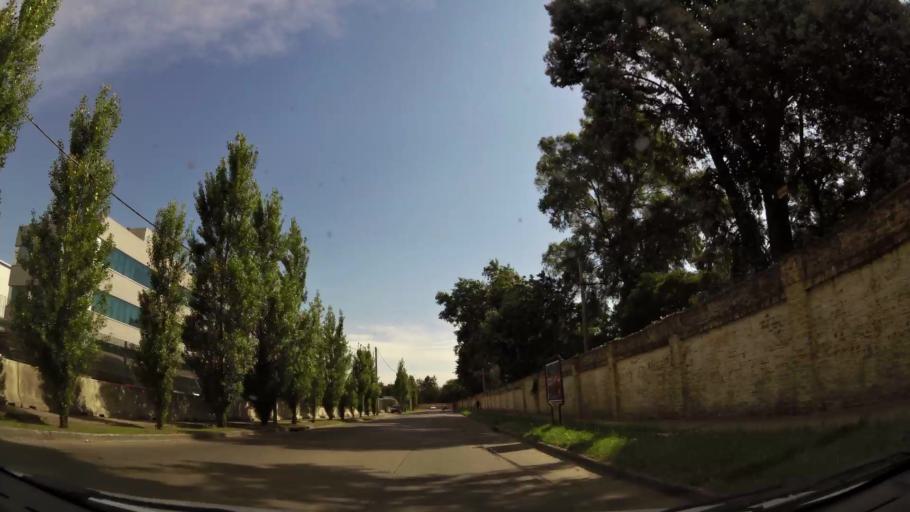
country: AR
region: Buenos Aires
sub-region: Partido de Merlo
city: Merlo
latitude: -34.6354
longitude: -58.7127
